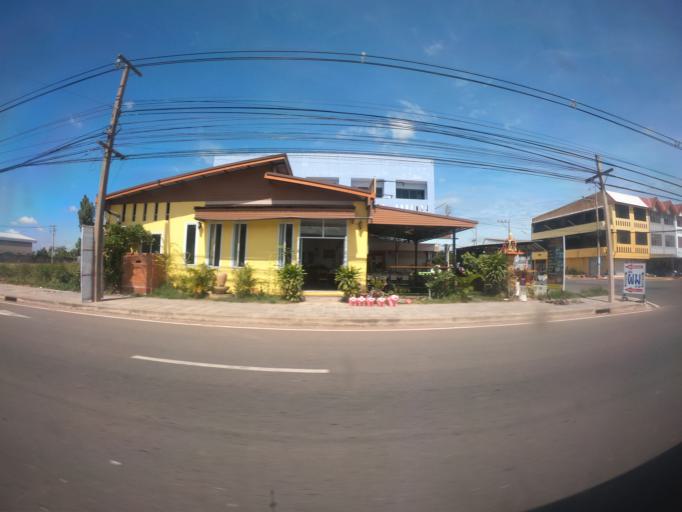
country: TH
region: Surin
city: Prasat
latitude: 14.6279
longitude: 103.4095
